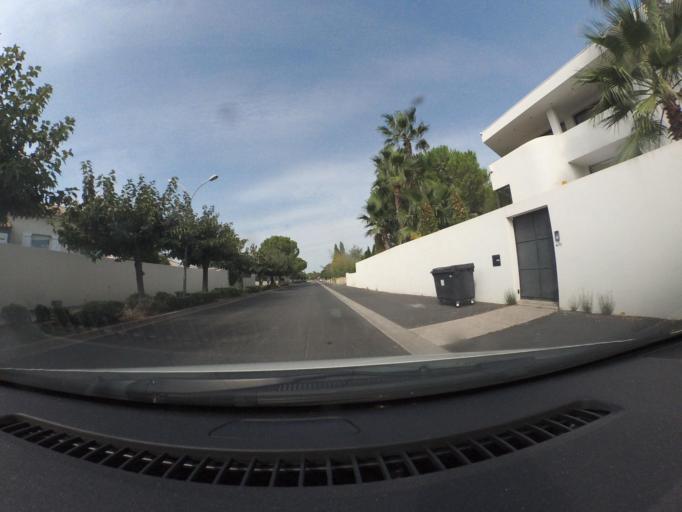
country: FR
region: Languedoc-Roussillon
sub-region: Departement de l'Herault
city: Baillargues
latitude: 43.6656
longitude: 4.0235
